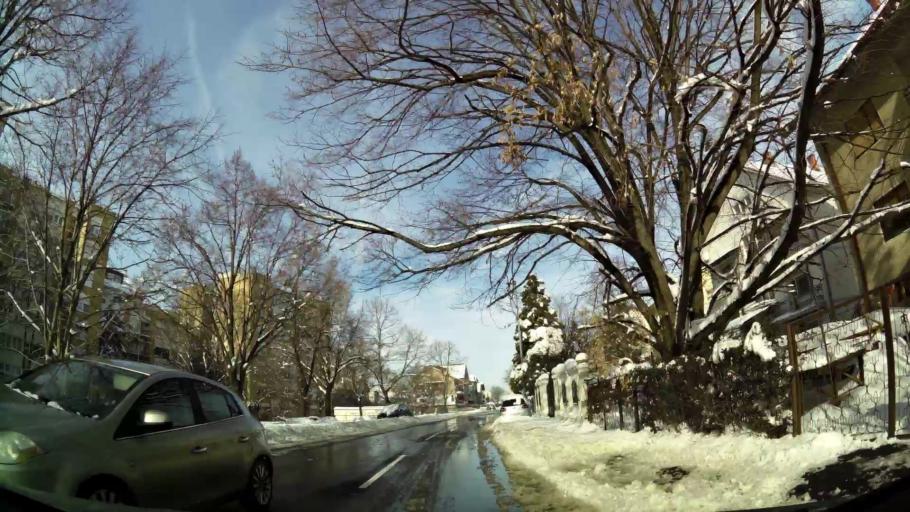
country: RS
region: Central Serbia
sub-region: Belgrade
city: Zvezdara
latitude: 44.7920
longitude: 20.5349
